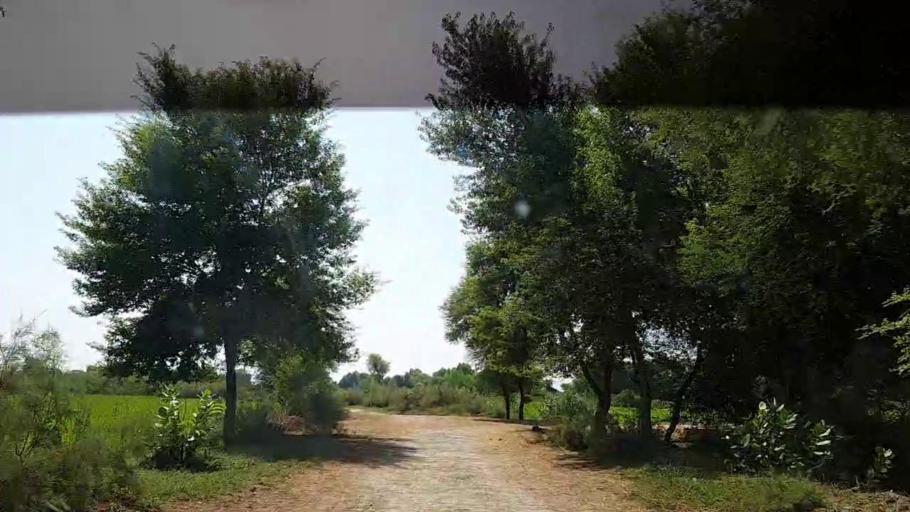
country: PK
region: Sindh
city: Ghauspur
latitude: 28.2126
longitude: 69.0864
